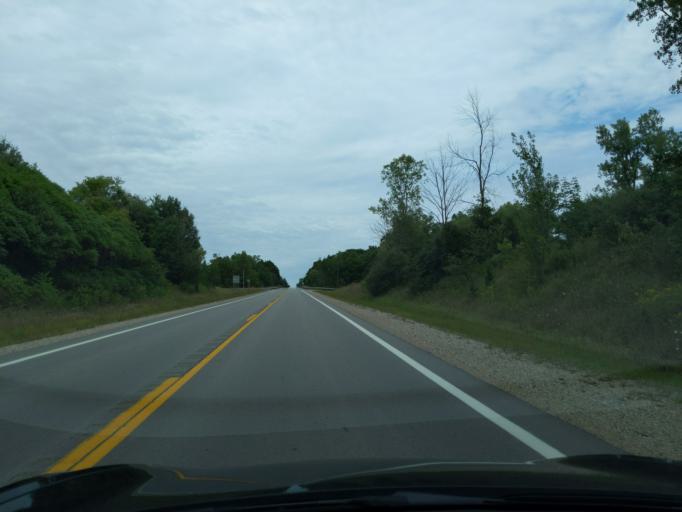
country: US
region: Michigan
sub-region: Barry County
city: Nashville
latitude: 42.5673
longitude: -85.0768
